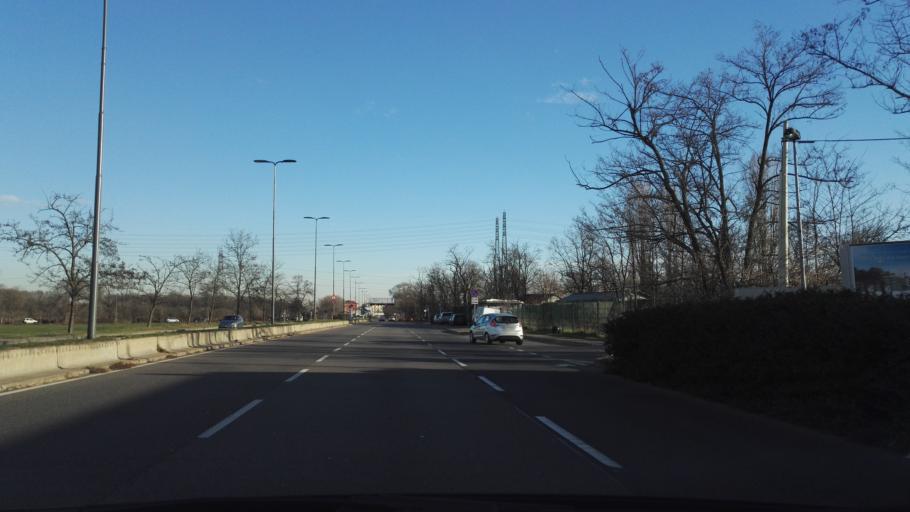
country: IT
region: Lombardy
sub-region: Citta metropolitana di Milano
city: Figino
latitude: 45.4860
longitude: 9.0806
